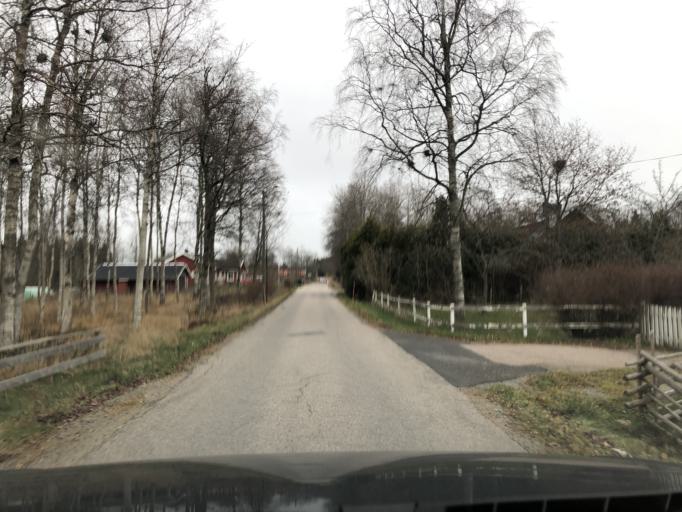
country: SE
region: Vaestra Goetaland
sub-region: Boras Kommun
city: Sjomarken
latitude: 57.7628
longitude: 12.8455
